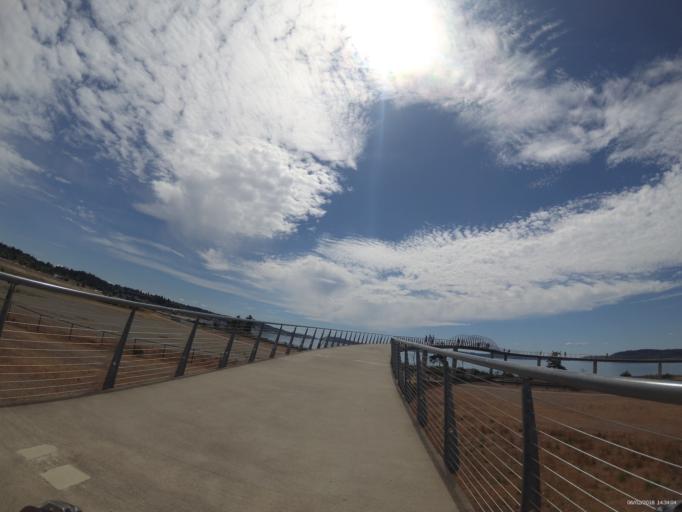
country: US
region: Washington
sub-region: Pierce County
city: Steilacoom
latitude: 47.2003
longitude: -122.5817
